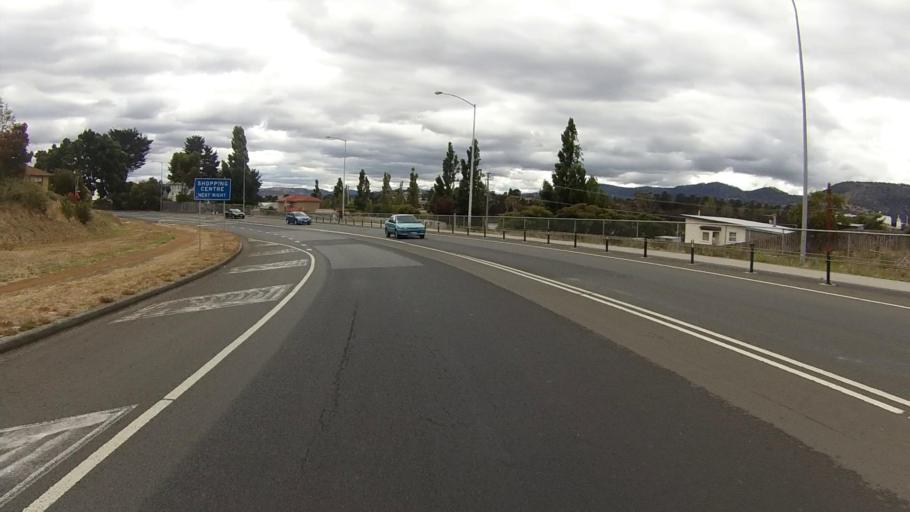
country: AU
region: Tasmania
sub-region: Glenorchy
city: Claremont
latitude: -42.7953
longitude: 147.2554
